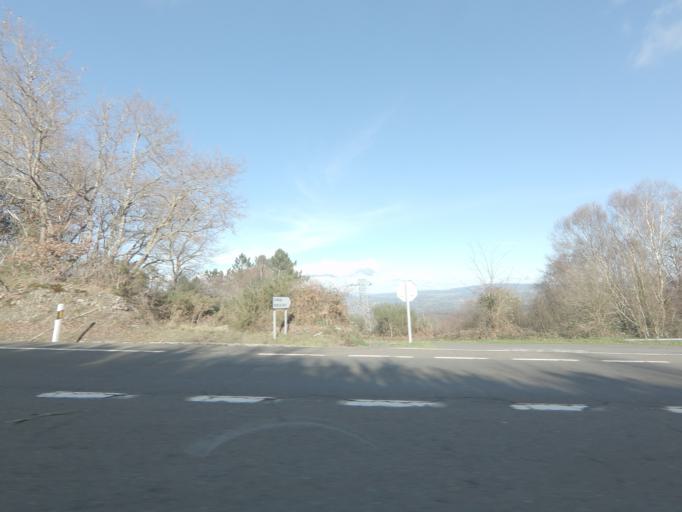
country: ES
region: Galicia
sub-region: Provincia de Pontevedra
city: Silleda
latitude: 42.7022
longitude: -8.3411
